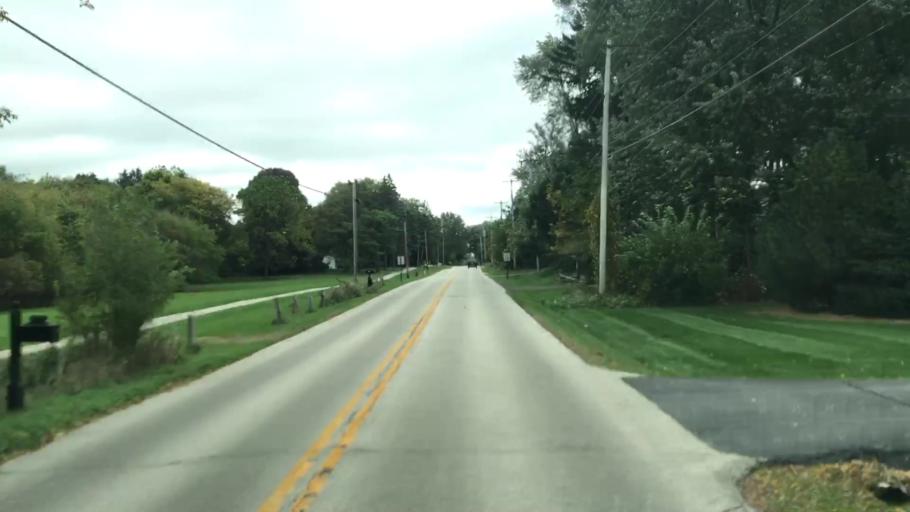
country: US
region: Wisconsin
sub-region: Waukesha County
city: Brookfield
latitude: 43.0758
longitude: -88.1373
